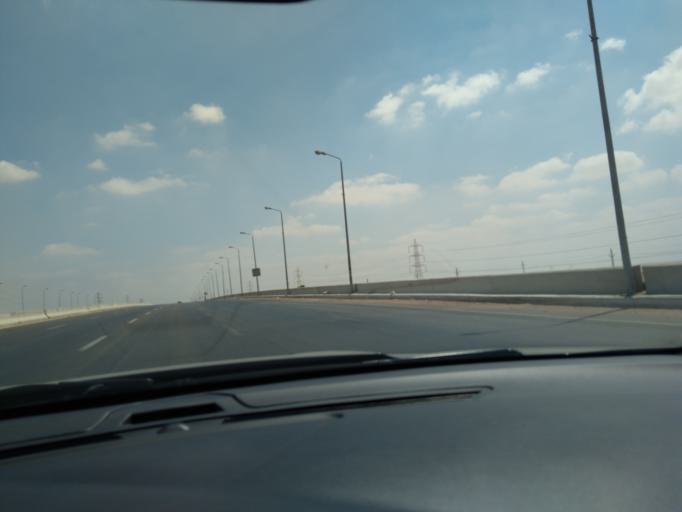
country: EG
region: Al Isma'iliyah
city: At Tall al Kabir
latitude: 30.3668
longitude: 31.9176
